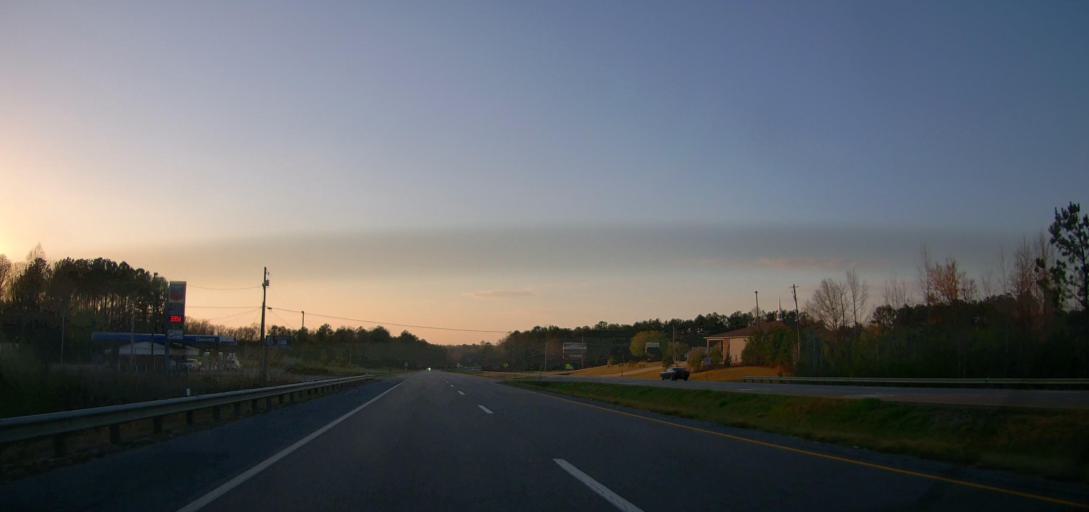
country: US
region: Alabama
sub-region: Coosa County
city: Stewartville
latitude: 33.1101
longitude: -86.2332
